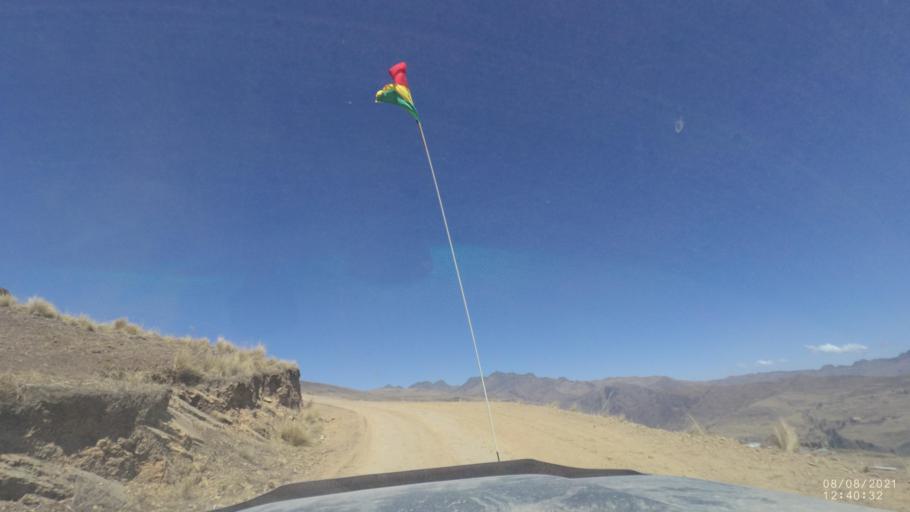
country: BO
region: Cochabamba
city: Colchani
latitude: -16.8290
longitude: -66.6232
